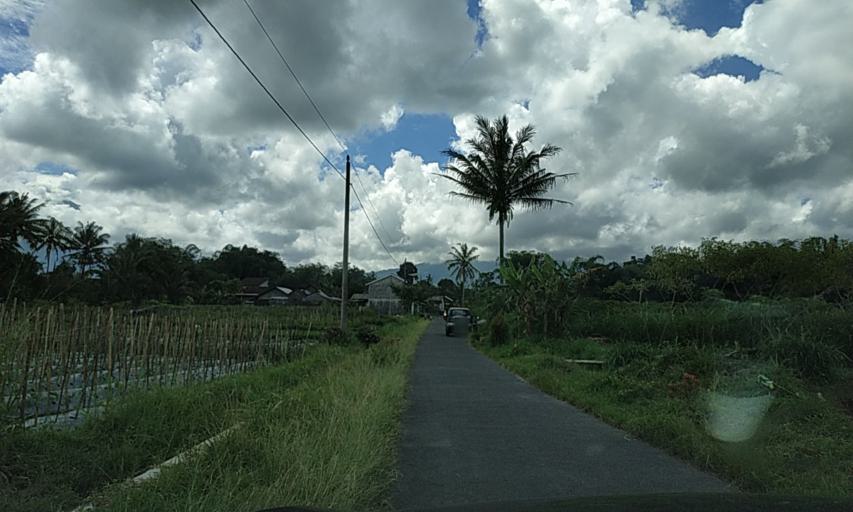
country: ID
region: Central Java
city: Muntilan
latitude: -7.5396
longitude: 110.3506
